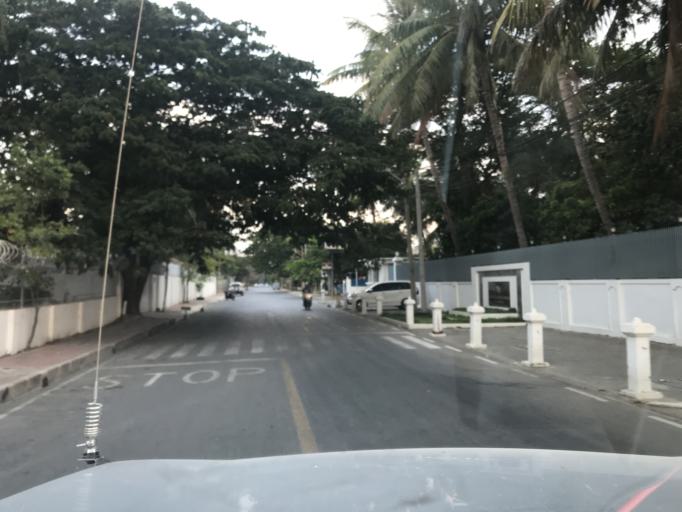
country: TL
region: Dili
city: Dili
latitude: -8.5499
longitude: 125.5651
